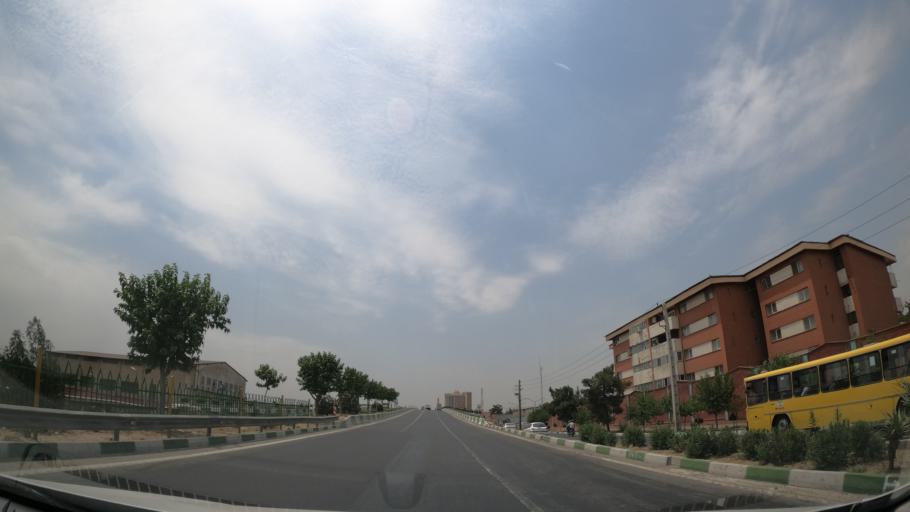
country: IR
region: Tehran
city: Tehran
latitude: 35.6755
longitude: 51.3114
